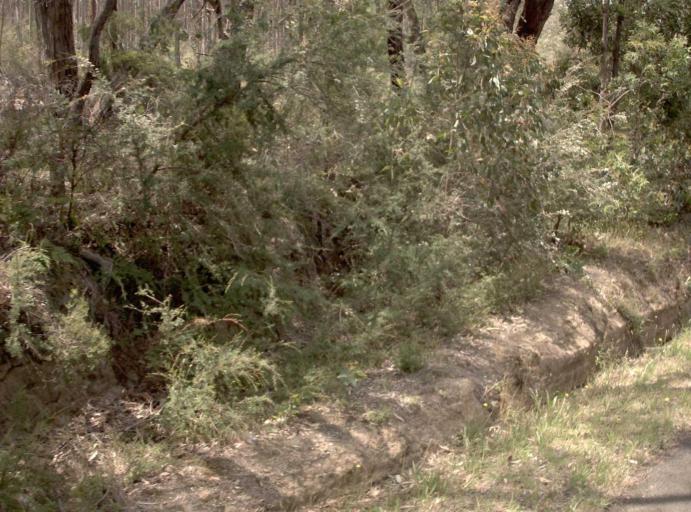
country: AU
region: Victoria
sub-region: Latrobe
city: Traralgon
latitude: -38.2815
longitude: 146.6941
